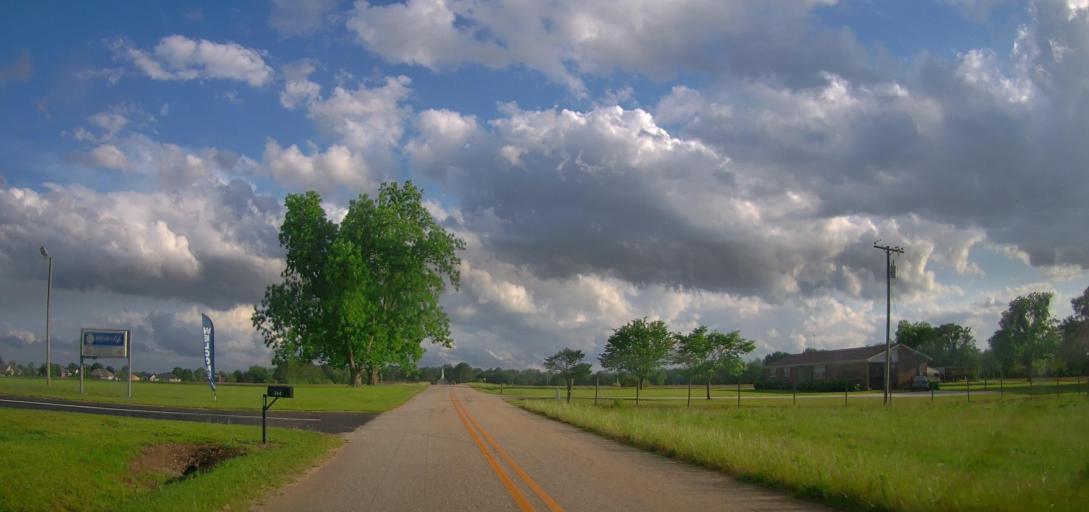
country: US
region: Georgia
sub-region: Peach County
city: Byron
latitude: 32.6100
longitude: -83.7734
